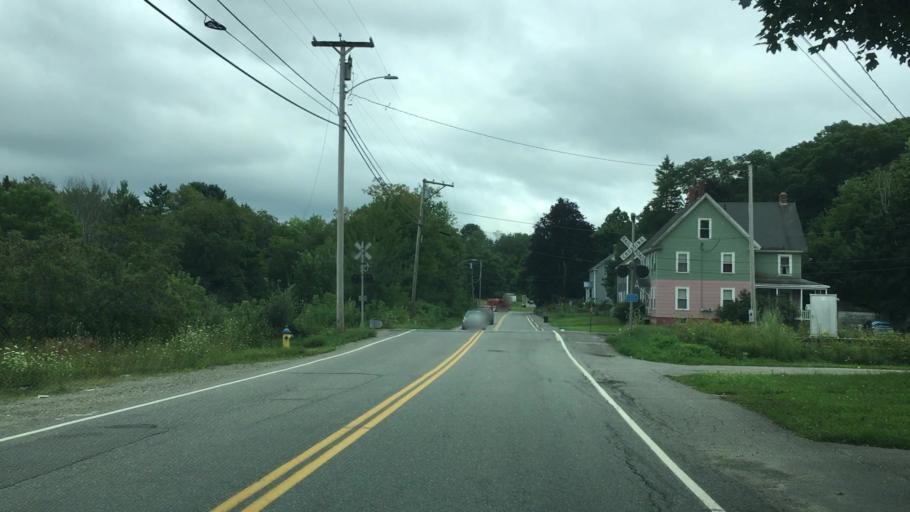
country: US
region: Maine
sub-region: Penobscot County
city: Bangor
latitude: 44.7681
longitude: -68.7815
